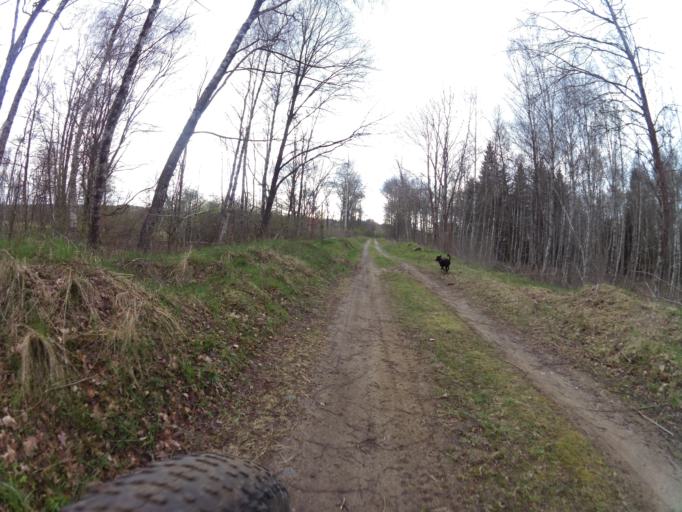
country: PL
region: West Pomeranian Voivodeship
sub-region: Powiat slawienski
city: Slawno
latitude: 54.3304
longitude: 16.7316
